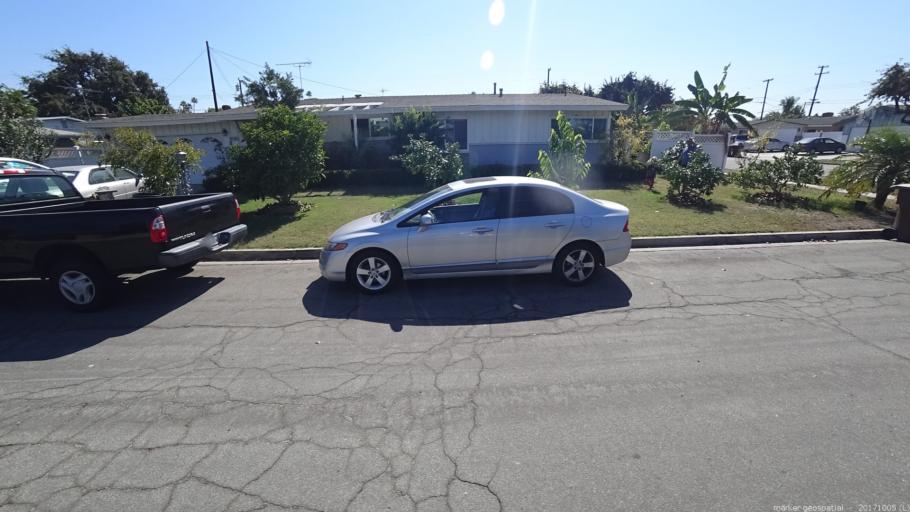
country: US
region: California
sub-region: Orange County
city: Stanton
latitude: 33.7947
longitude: -117.9736
